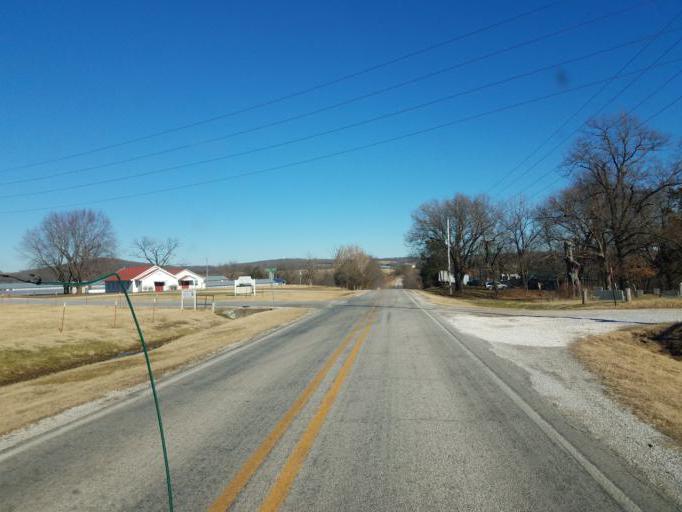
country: US
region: Arkansas
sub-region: Washington County
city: Elkins
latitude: 36.0335
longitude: -93.9730
